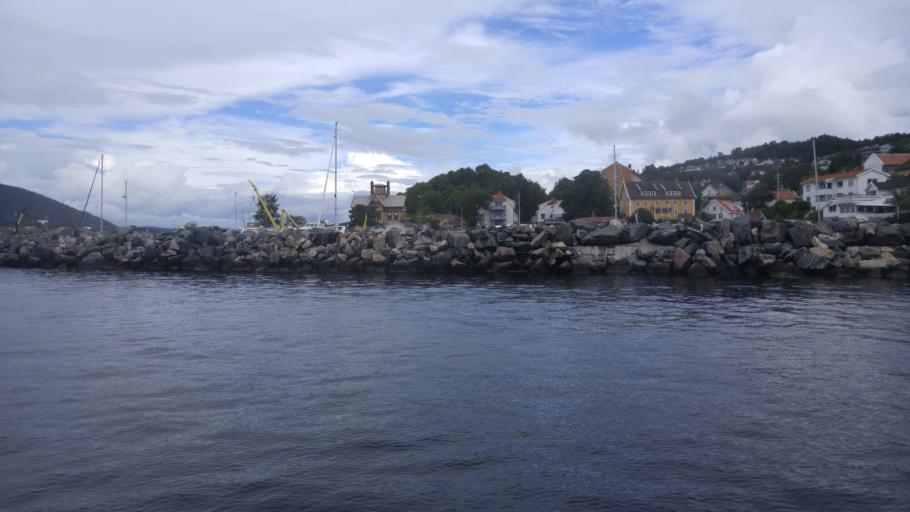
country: NO
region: Akershus
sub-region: Frogn
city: Drobak
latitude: 59.6614
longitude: 10.6268
